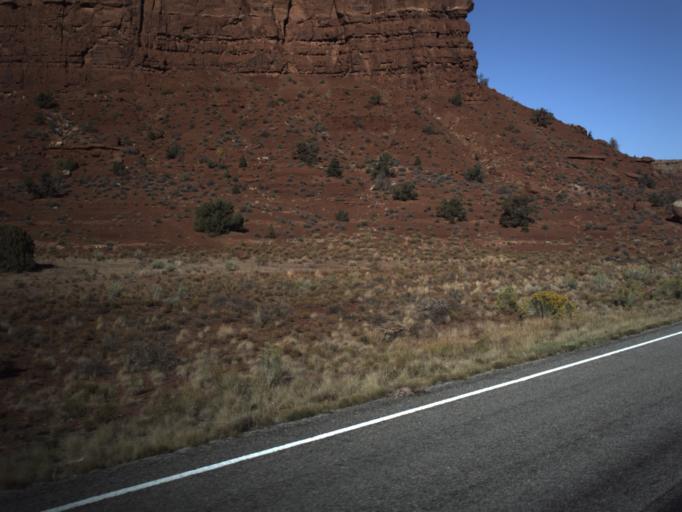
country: US
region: Utah
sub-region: San Juan County
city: Blanding
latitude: 37.6884
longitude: -110.2237
